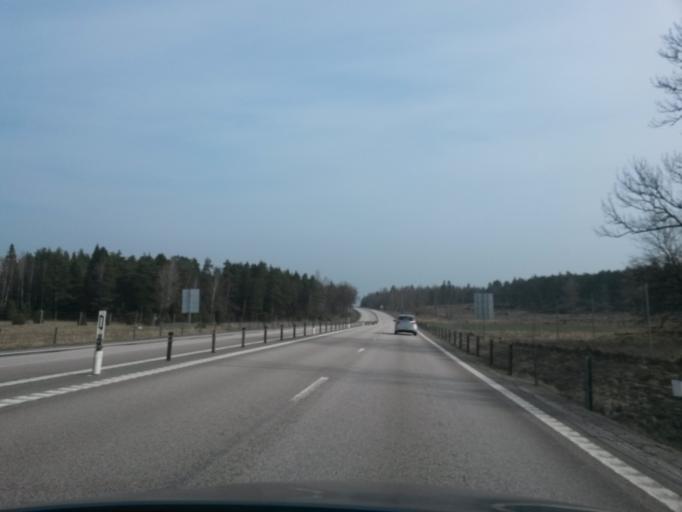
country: SE
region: Vaestra Goetaland
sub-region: Toreboda Kommun
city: Toereboda
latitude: 58.7663
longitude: 13.9835
